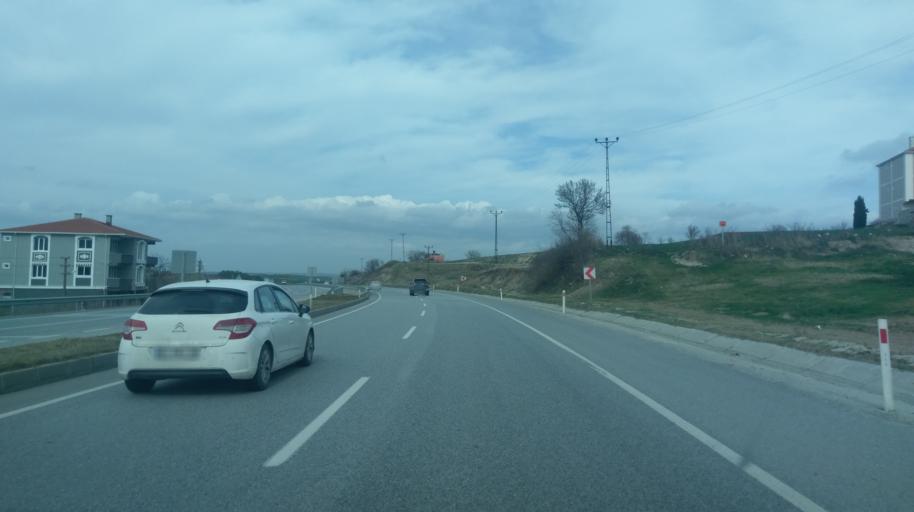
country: TR
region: Edirne
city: Kircasalih
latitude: 41.3970
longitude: 26.8089
